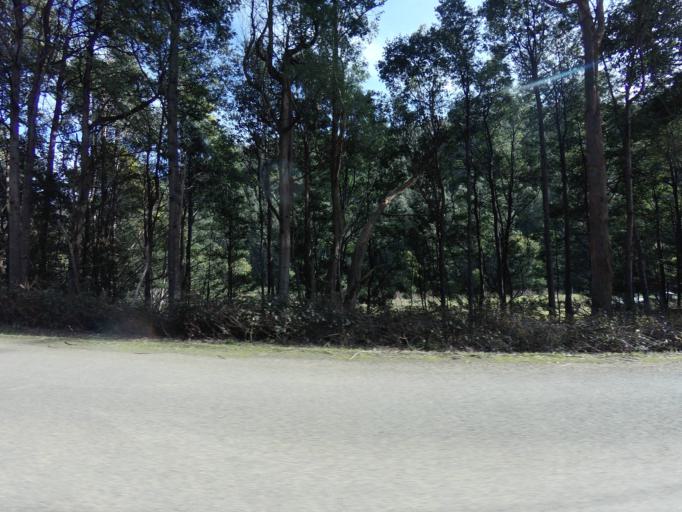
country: AU
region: Tasmania
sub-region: Huon Valley
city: Huonville
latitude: -43.0372
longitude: 147.1393
